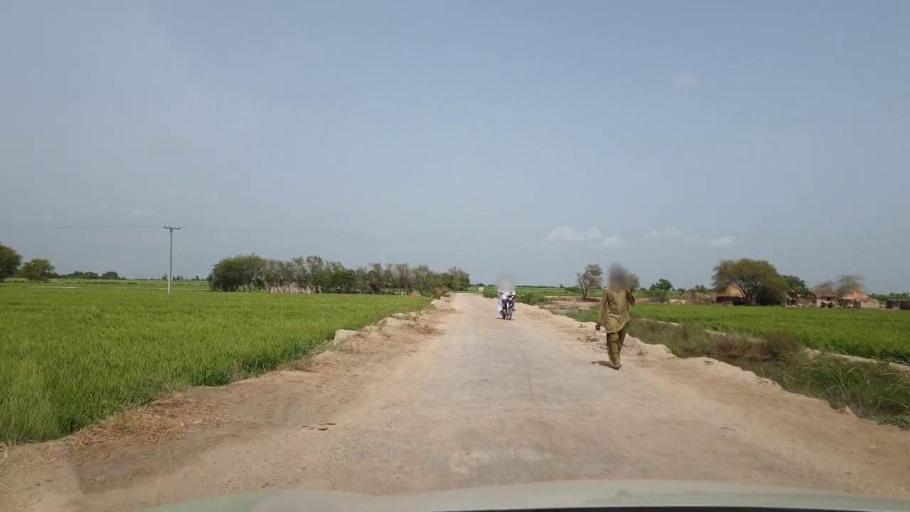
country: PK
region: Sindh
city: Mirwah Gorchani
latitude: 25.2560
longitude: 68.9697
